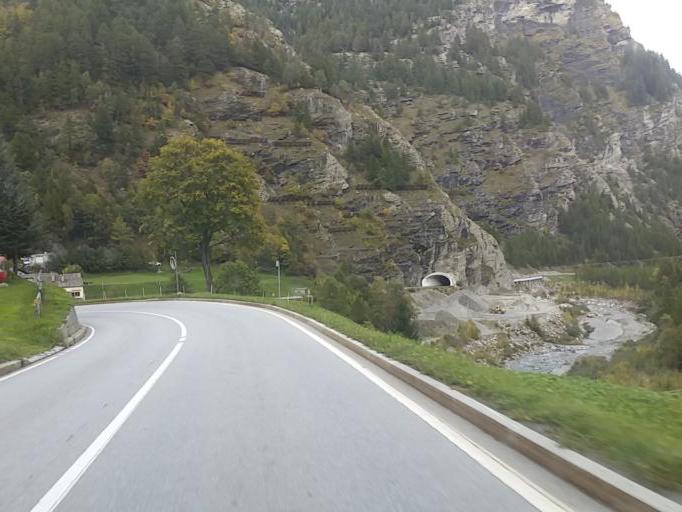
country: IT
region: Piedmont
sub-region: Provincia Verbano-Cusio-Ossola
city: Antronapiana
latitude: 46.1826
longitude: 8.0727
